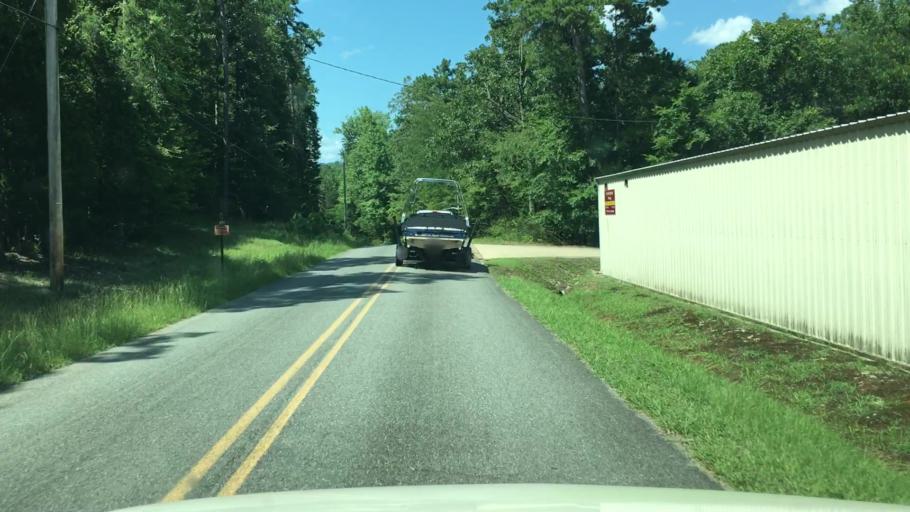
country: US
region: Arkansas
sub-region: Garland County
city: Piney
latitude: 34.5255
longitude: -93.3359
